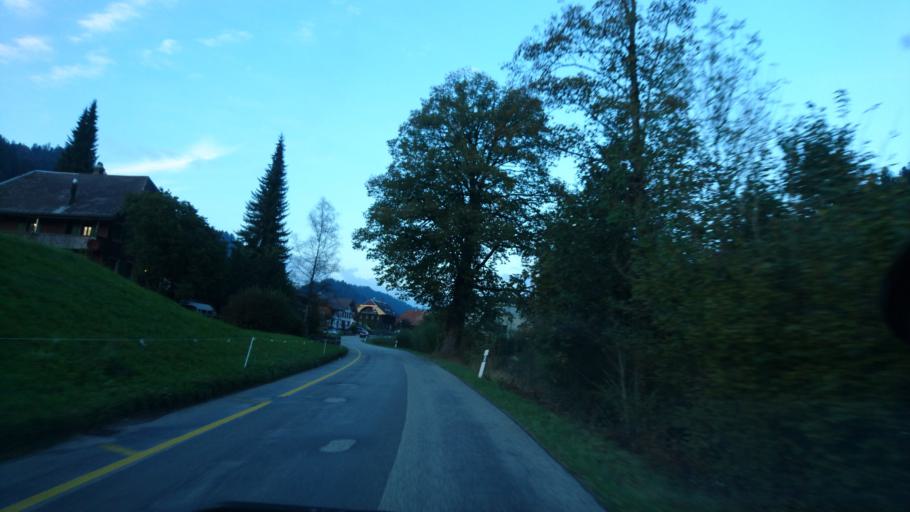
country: CH
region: Bern
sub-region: Emmental District
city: Trub
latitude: 46.9417
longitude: 7.8828
